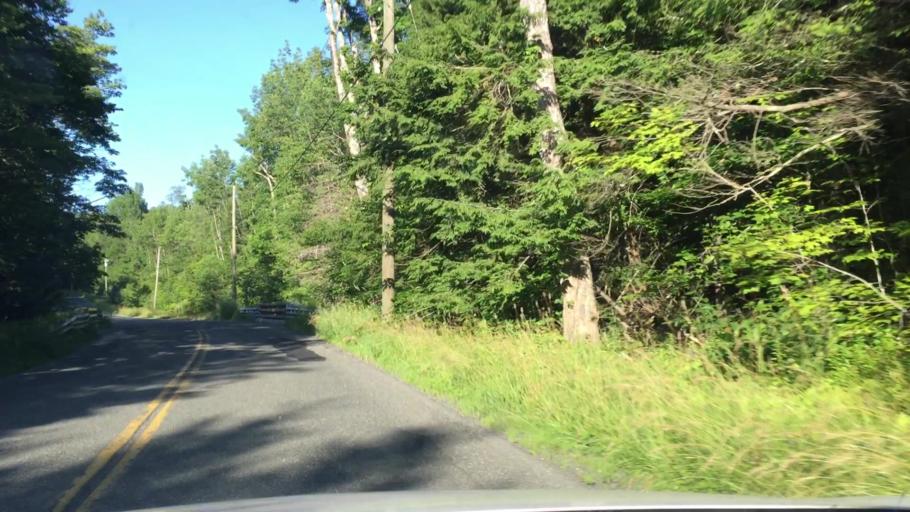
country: US
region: Massachusetts
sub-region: Berkshire County
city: Becket
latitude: 42.3116
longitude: -73.1225
